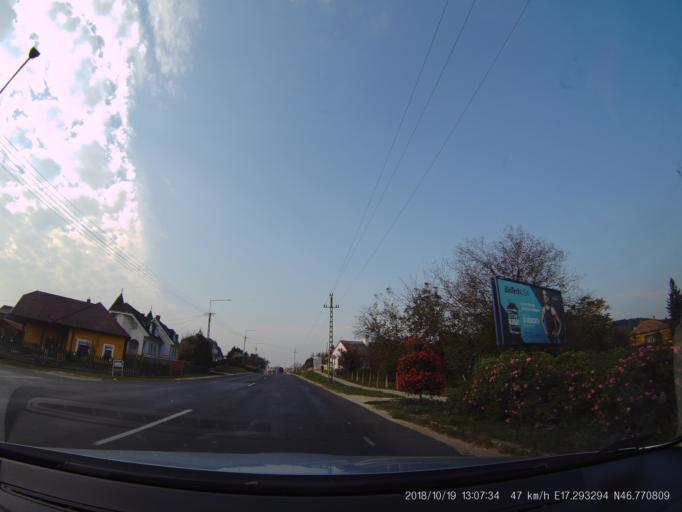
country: HU
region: Zala
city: Gyenesdias
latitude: 46.7708
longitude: 17.2932
